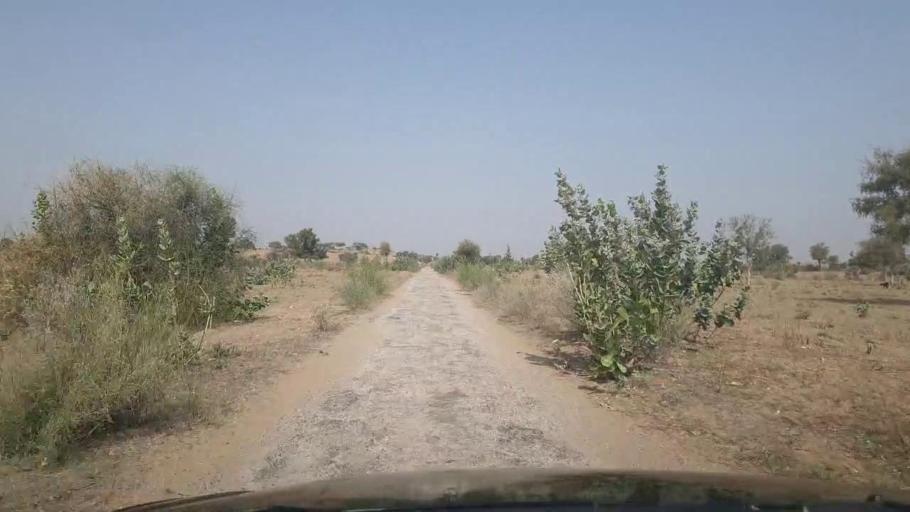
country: PK
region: Sindh
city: Islamkot
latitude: 25.0616
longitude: 70.2062
